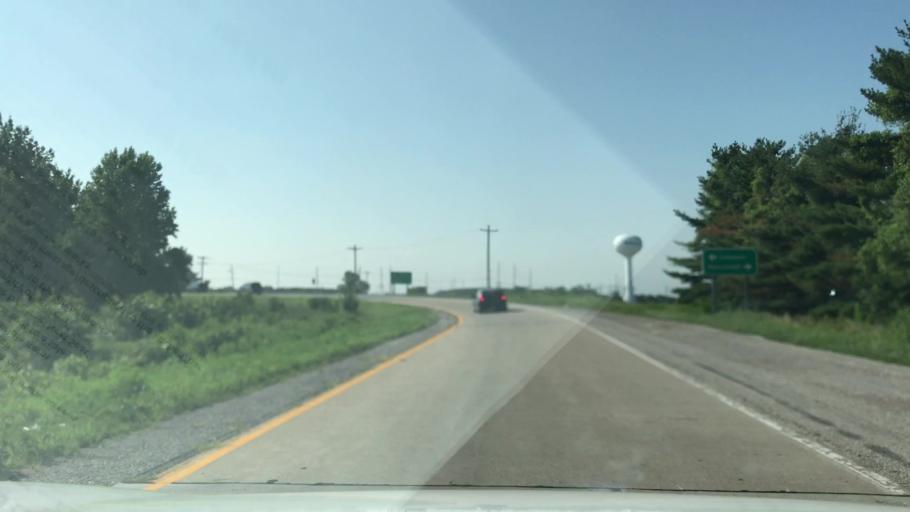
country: US
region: Illinois
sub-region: Saint Clair County
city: Scott Air Force Base
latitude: 38.5507
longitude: -89.8091
